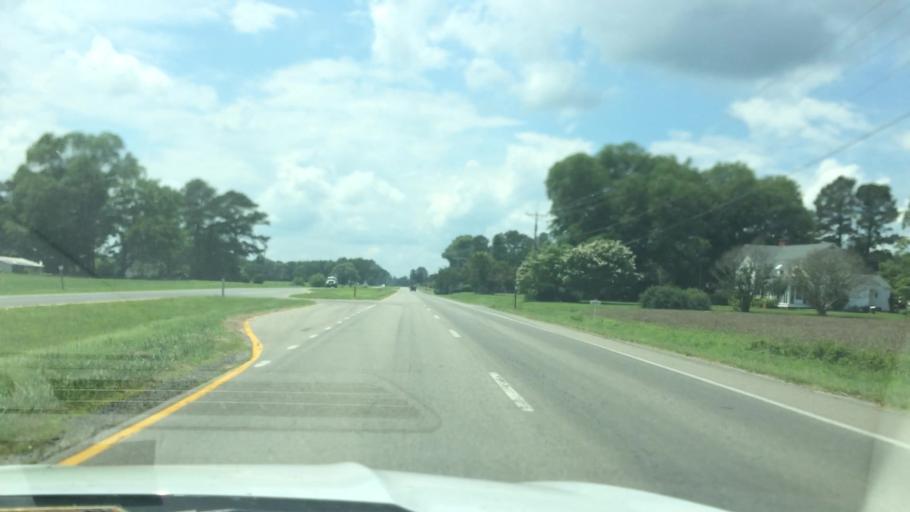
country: US
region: Virginia
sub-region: King William County
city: West Point
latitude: 37.5447
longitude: -76.7078
